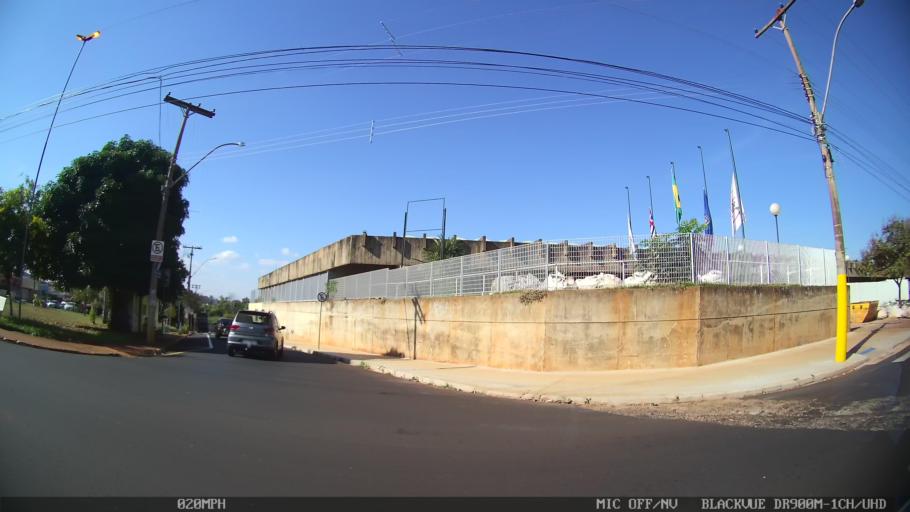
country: BR
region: Sao Paulo
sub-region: Ribeirao Preto
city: Ribeirao Preto
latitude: -21.1901
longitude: -47.7780
